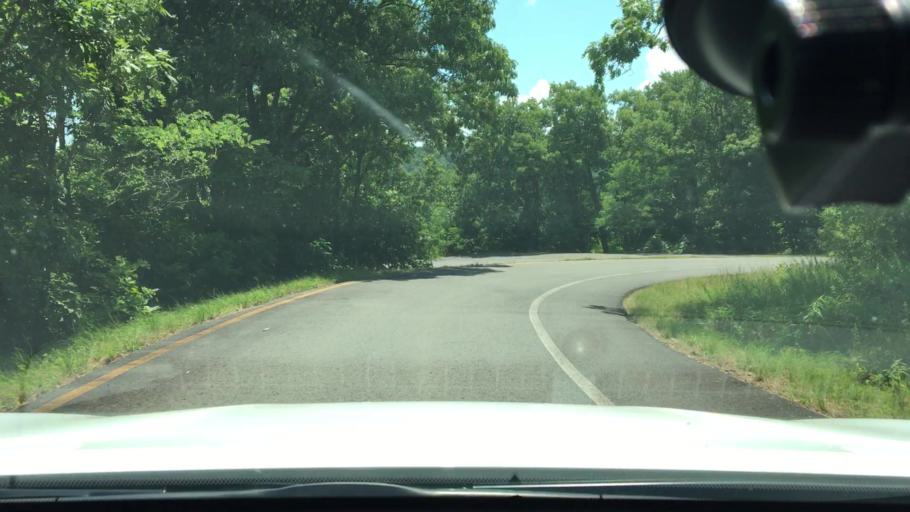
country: US
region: Arkansas
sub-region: Logan County
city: Paris
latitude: 35.1743
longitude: -93.6416
